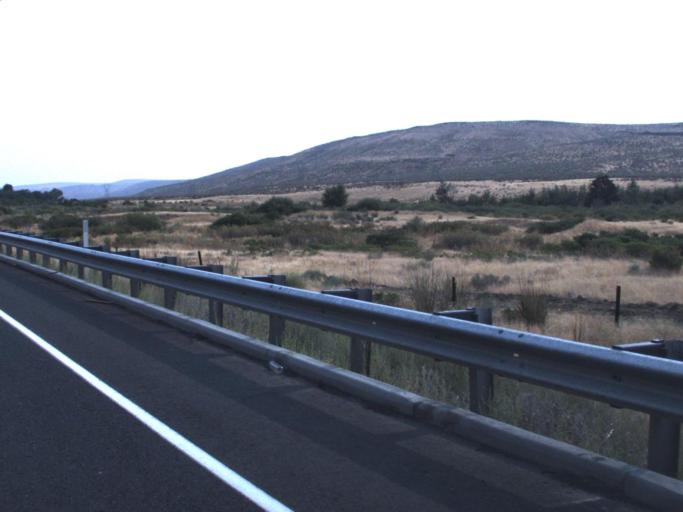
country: US
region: Washington
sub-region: Yakima County
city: Toppenish
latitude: 46.1999
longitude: -120.4847
